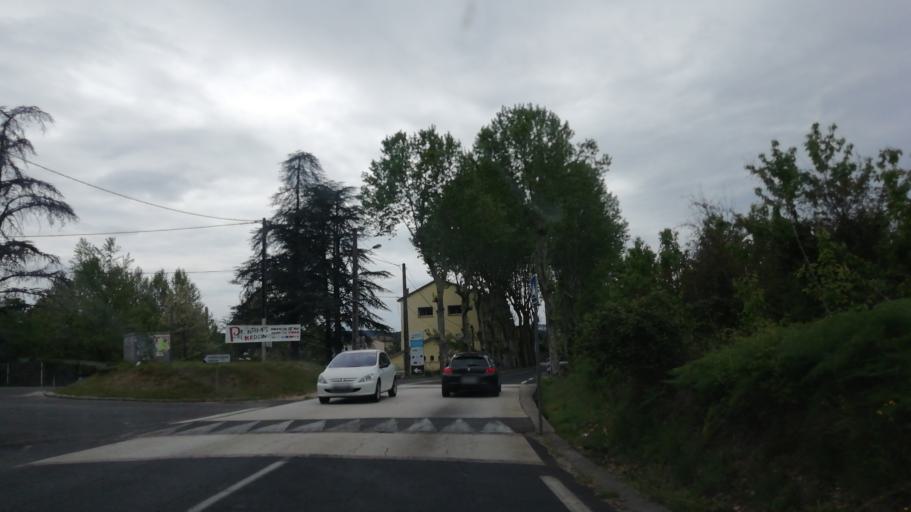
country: FR
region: Languedoc-Roussillon
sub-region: Departement de l'Herault
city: Saint-Bauzille-de-Putois
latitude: 43.9041
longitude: 3.7380
